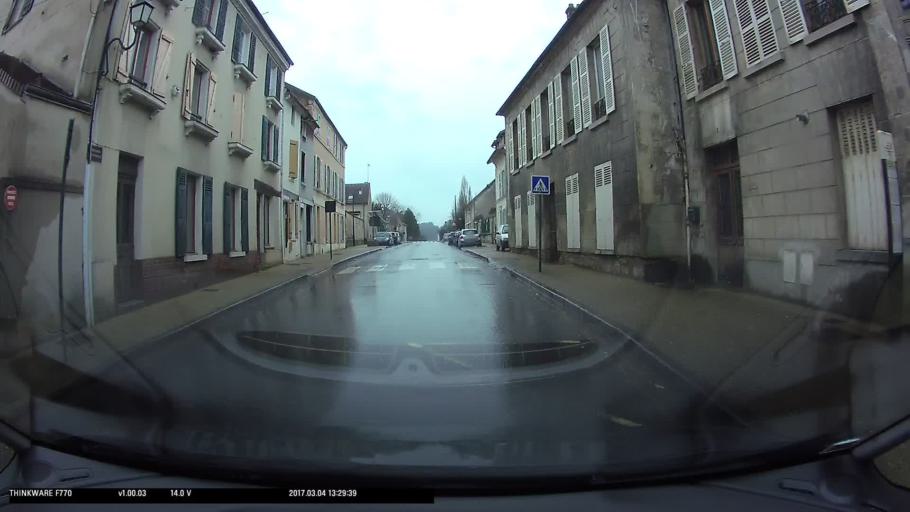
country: FR
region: Ile-de-France
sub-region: Departement du Val-d'Oise
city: Marines
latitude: 49.1430
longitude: 1.9808
